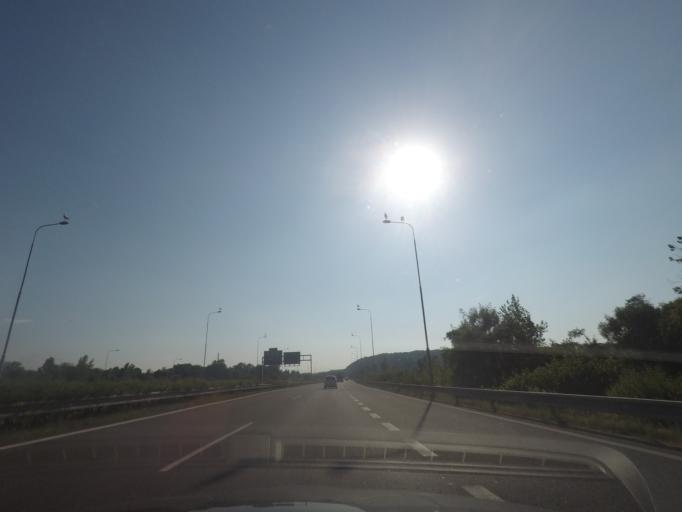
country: CZ
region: Moravskoslezsky
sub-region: Okres Ostrava-Mesto
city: Ostrava
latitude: 49.8737
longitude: 18.2968
